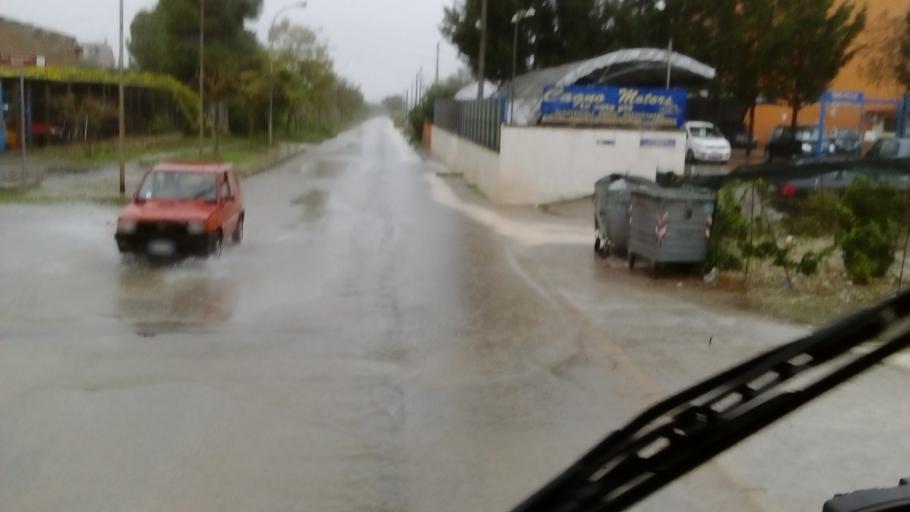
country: IT
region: Sicily
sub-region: Enna
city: Pietraperzia
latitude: 37.4135
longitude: 14.1421
